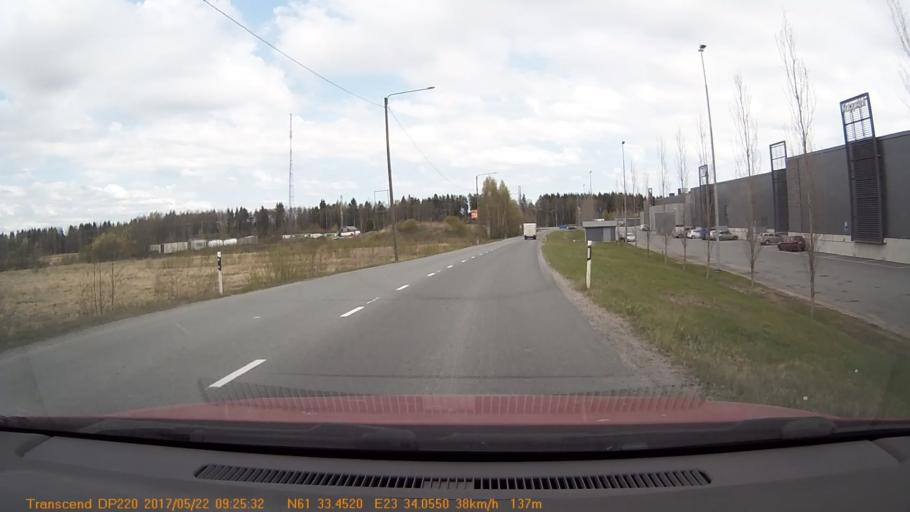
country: FI
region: Pirkanmaa
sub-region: Tampere
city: Yloejaervi
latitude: 61.5575
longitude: 23.5674
